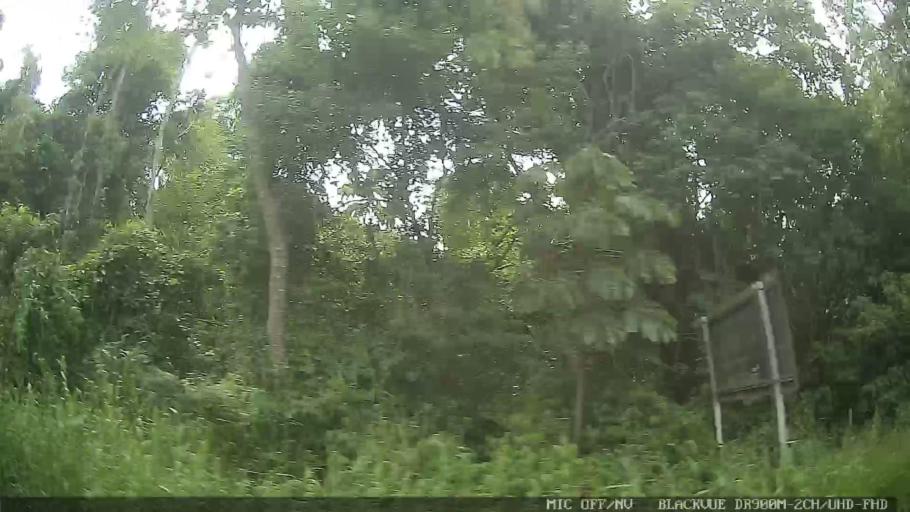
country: BR
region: Sao Paulo
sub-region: Suzano
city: Suzano
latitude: -23.4826
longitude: -46.2602
